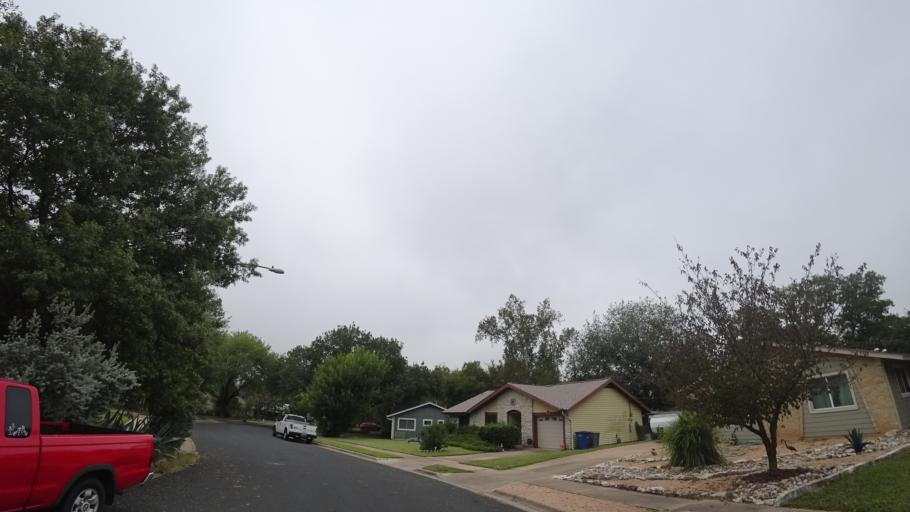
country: US
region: Texas
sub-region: Travis County
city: Austin
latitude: 30.2115
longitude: -97.7758
